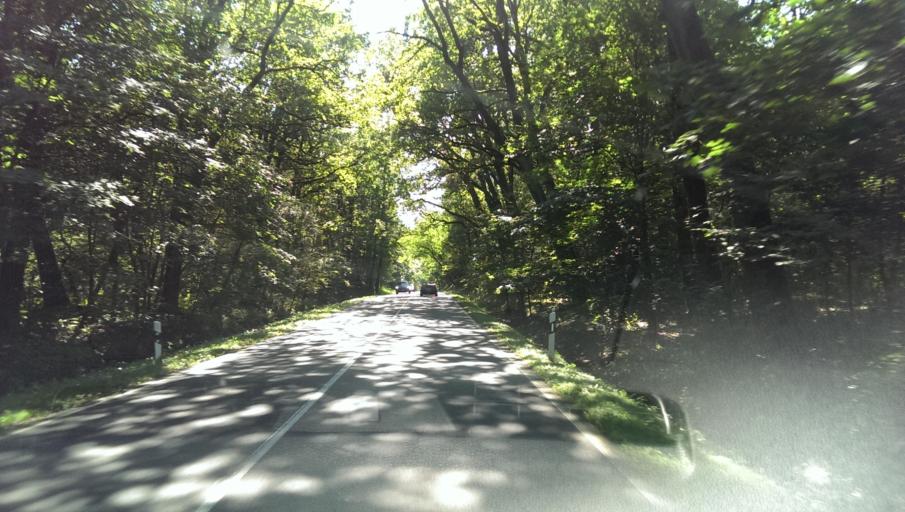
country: DE
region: Saxony-Anhalt
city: Kropstadt
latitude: 51.9385
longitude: 12.7177
